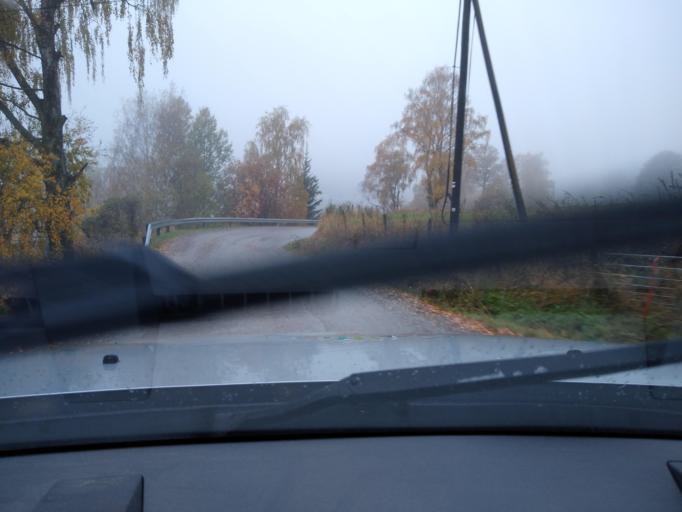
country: NO
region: Oppland
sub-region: Ringebu
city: Ringebu
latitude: 61.5299
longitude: 10.1533
